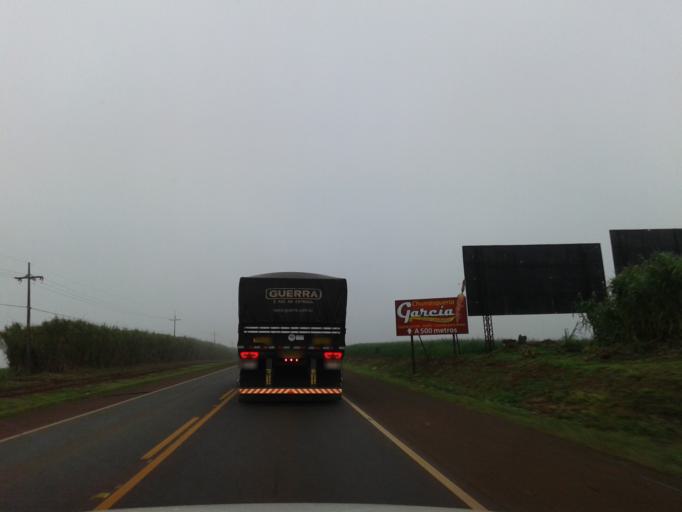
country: PY
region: Itapua
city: Pirapo
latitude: -26.8694
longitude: -55.4593
